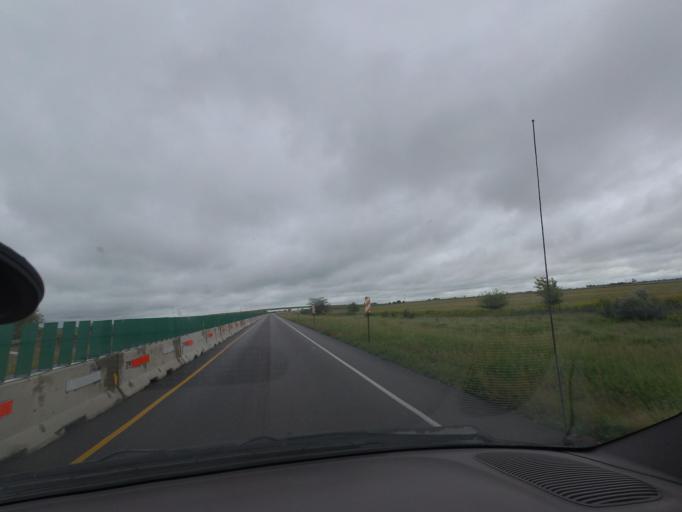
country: US
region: Illinois
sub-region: Piatt County
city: Cerro Gordo
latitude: 40.0074
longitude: -88.7746
